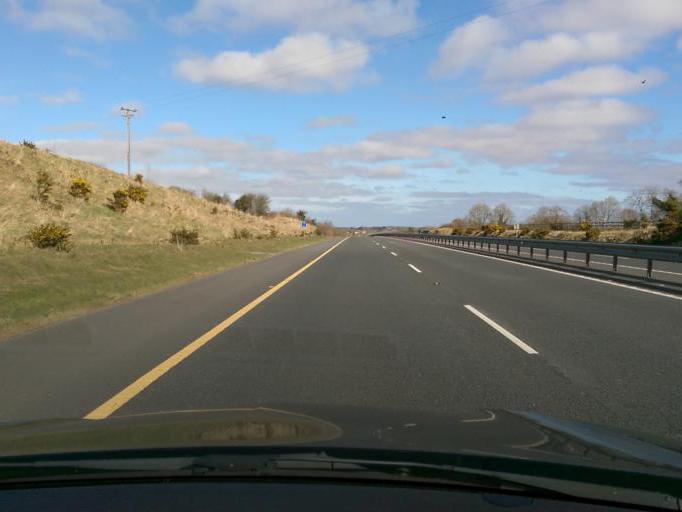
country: IE
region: Leinster
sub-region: An Iarmhi
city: Athlone
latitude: 53.3843
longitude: -8.0508
